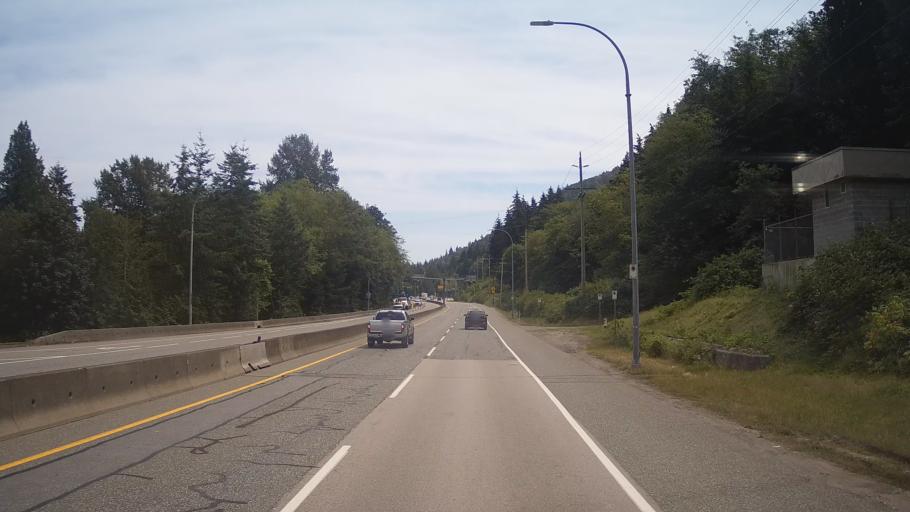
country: CA
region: British Columbia
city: Burnaby
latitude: 49.2902
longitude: -122.9322
